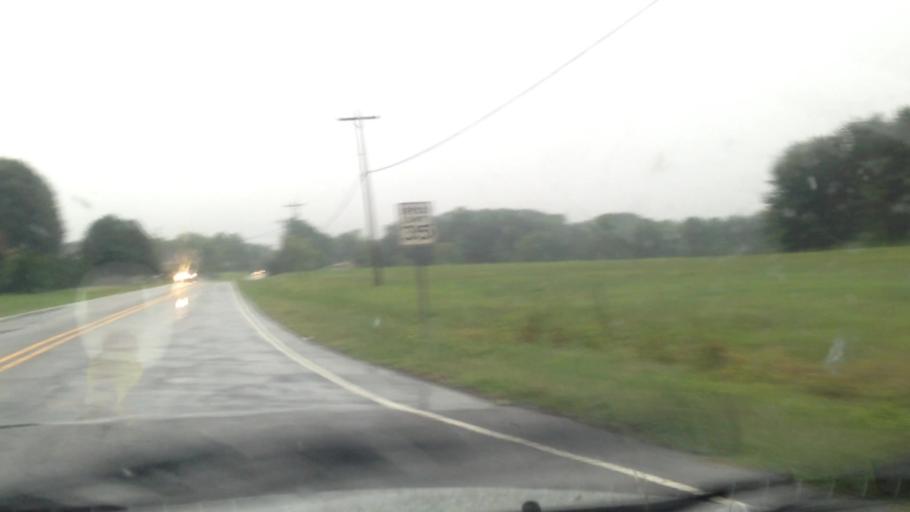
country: US
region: North Carolina
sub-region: Forsyth County
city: Kernersville
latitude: 36.1404
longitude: -80.0814
